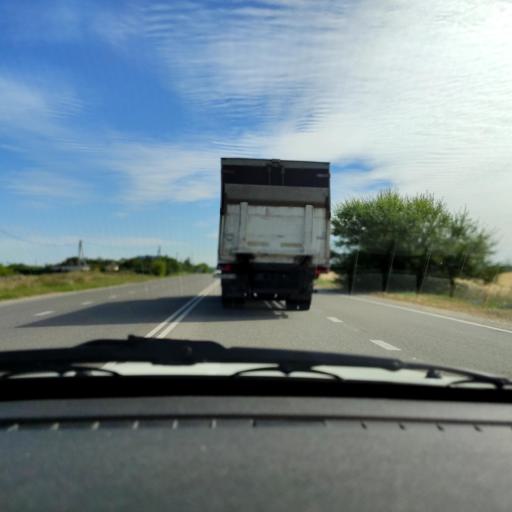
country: RU
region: Voronezj
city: Orlovo
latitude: 51.7361
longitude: 39.5662
